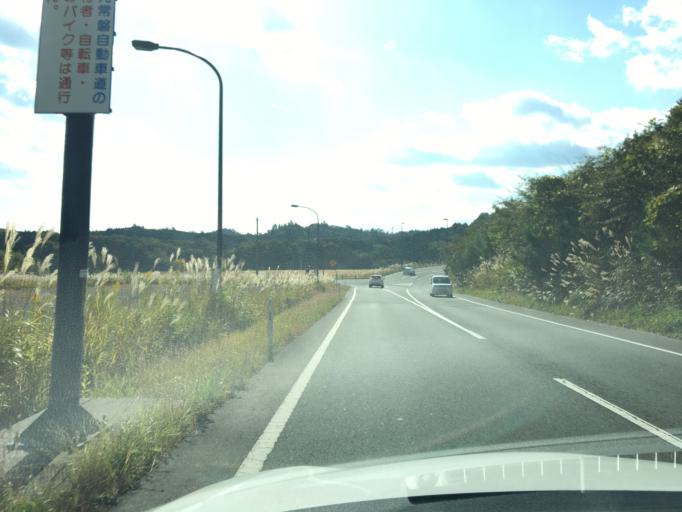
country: JP
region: Fukushima
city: Iwaki
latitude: 37.2349
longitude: 140.9893
